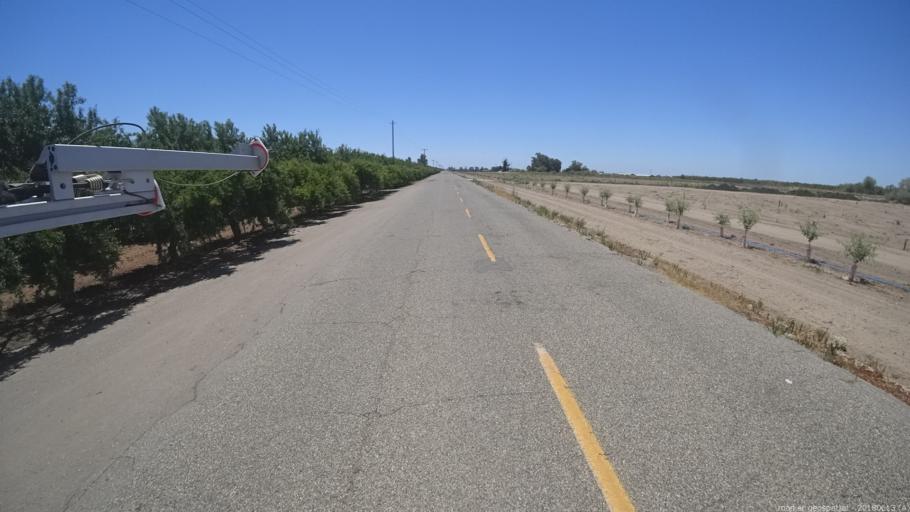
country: US
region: California
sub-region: Madera County
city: Fairmead
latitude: 36.9964
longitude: -120.1612
